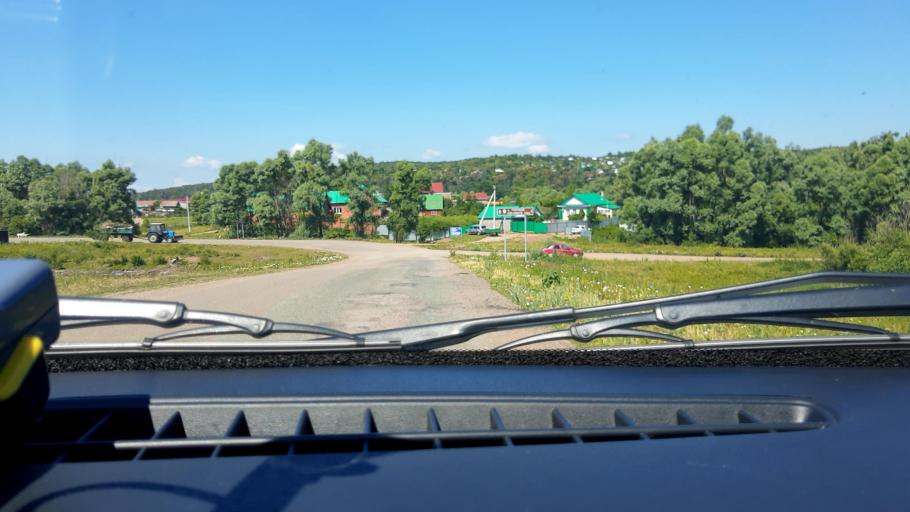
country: RU
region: Bashkortostan
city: Karmaskaly
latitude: 54.3563
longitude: 55.9031
